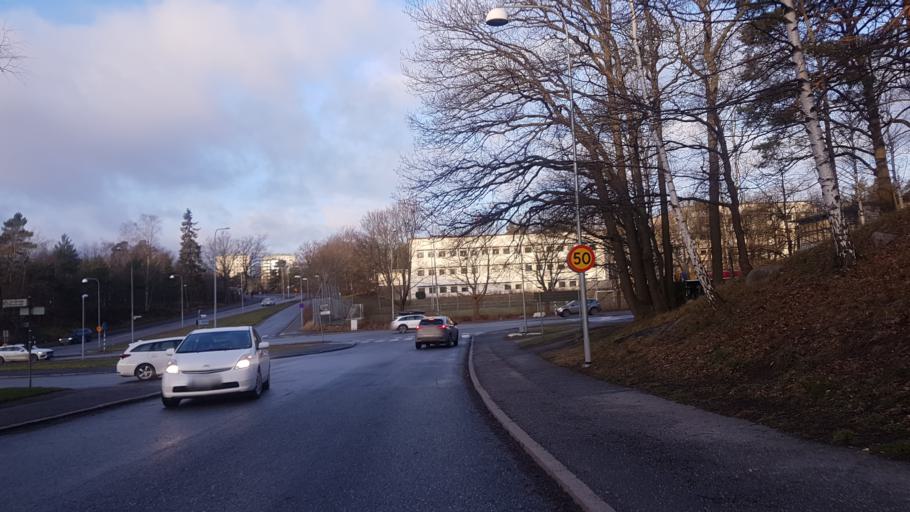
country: SE
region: Stockholm
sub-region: Lidingo
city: Lidingoe
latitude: 59.3515
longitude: 18.1497
